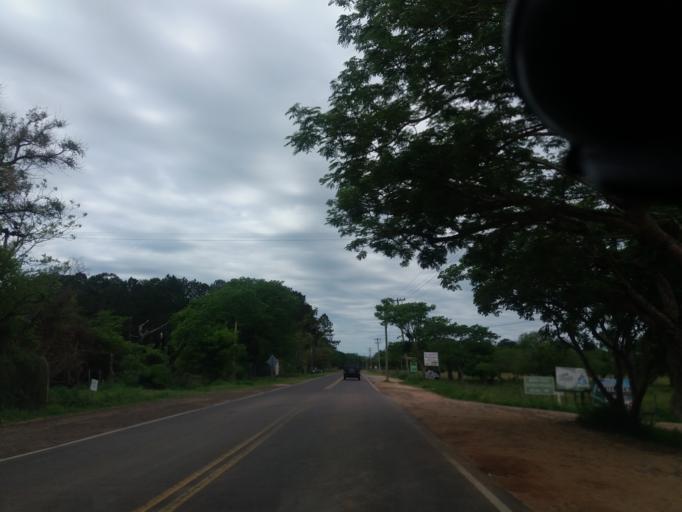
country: AR
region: Corrientes
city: Corrientes
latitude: -27.4515
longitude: -58.7315
